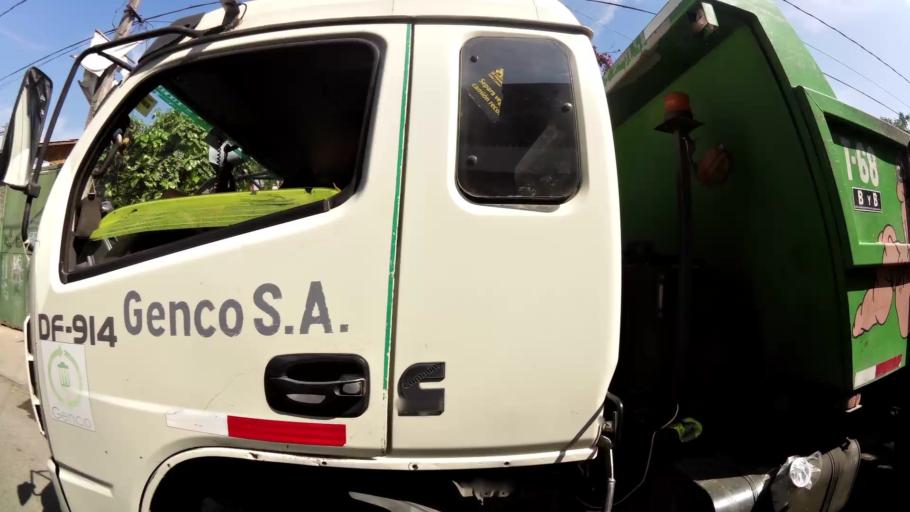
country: CL
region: Santiago Metropolitan
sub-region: Provincia de Santiago
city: La Pintana
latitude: -33.5600
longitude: -70.6498
